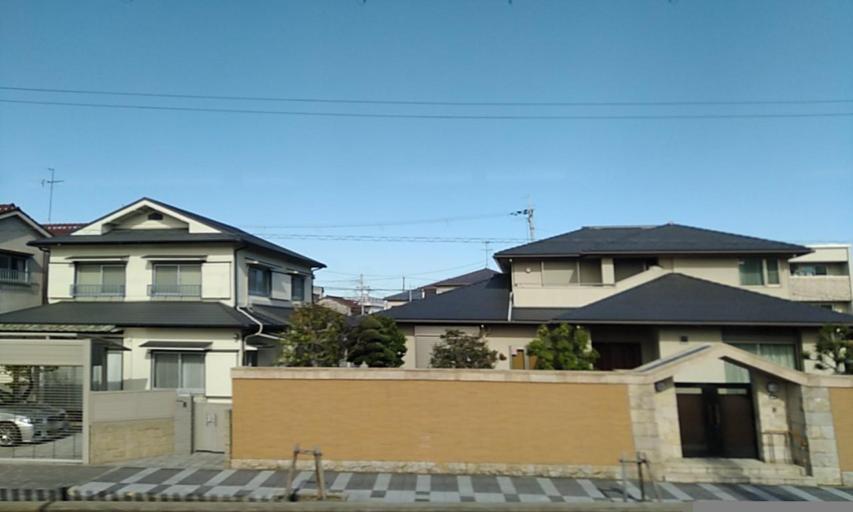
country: JP
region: Hyogo
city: Itami
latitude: 34.7531
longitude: 135.4191
